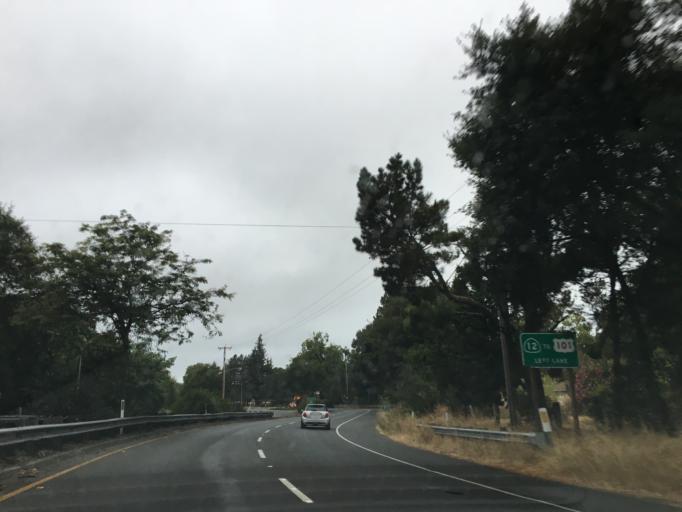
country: US
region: California
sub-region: Sonoma County
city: Santa Rosa
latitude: 38.4495
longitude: -122.6849
